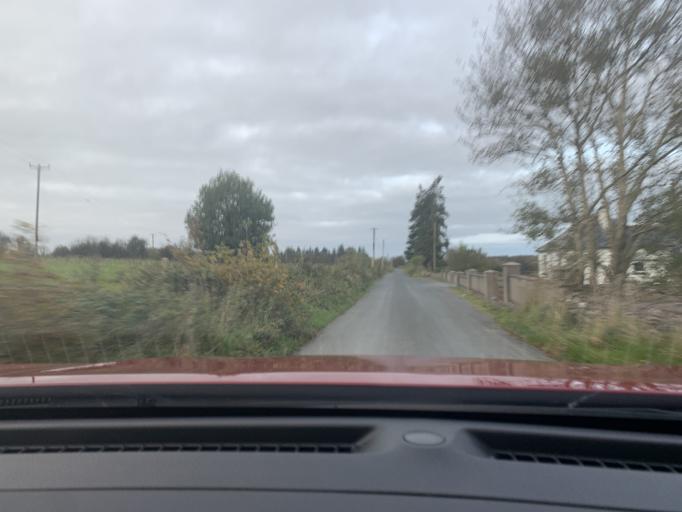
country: IE
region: Connaught
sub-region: Sligo
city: Tobercurry
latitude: 54.0562
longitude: -8.6864
